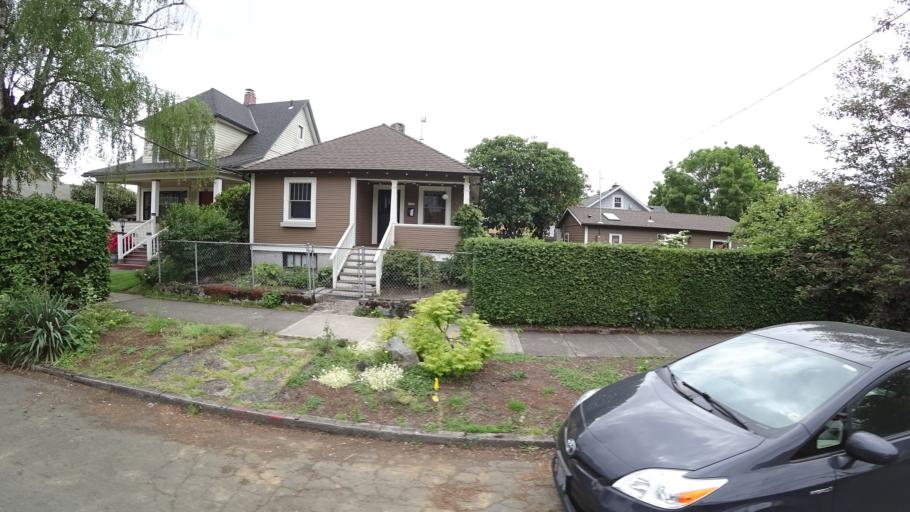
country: US
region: Oregon
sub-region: Multnomah County
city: Portland
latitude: 45.5110
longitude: -122.6182
